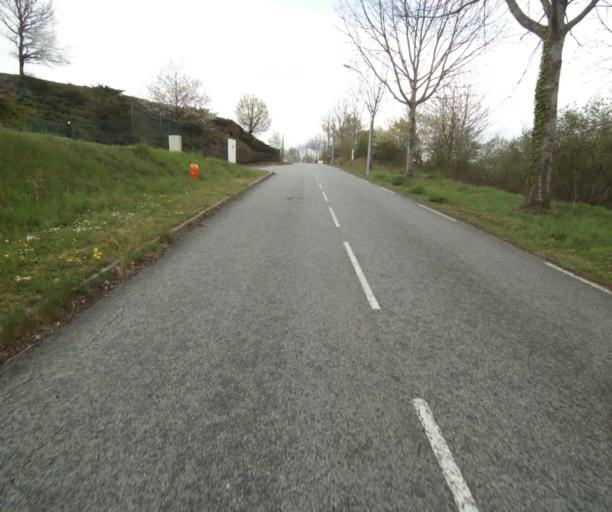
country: FR
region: Limousin
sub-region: Departement de la Correze
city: Tulle
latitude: 45.2806
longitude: 1.7941
